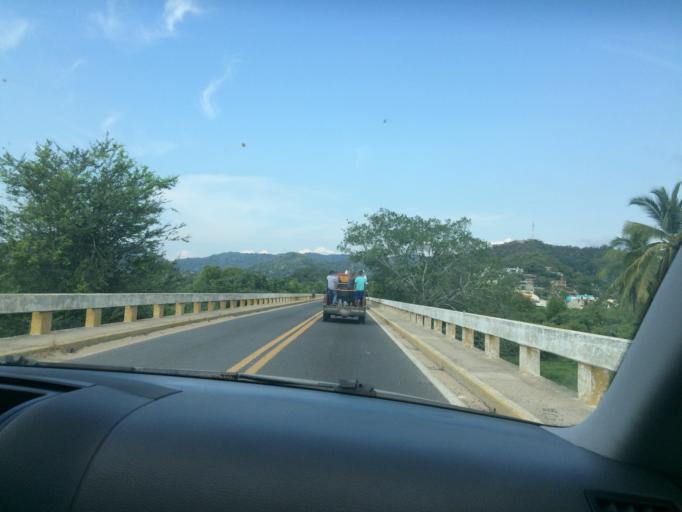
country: MX
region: Jalisco
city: Cihuatlan
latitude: 19.2355
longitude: -104.5523
